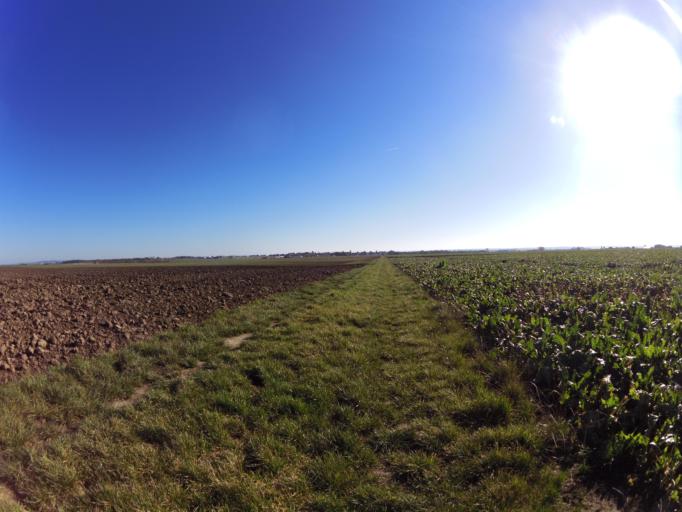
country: DE
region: Bavaria
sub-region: Regierungsbezirk Unterfranken
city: Giebelstadt
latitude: 49.6695
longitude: 9.9343
